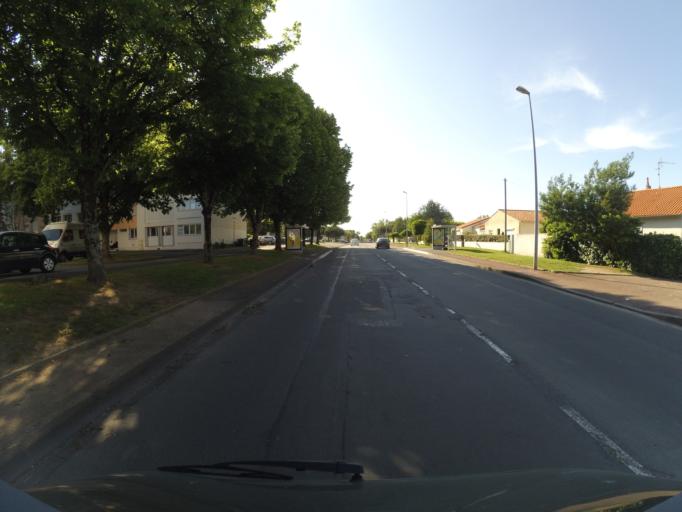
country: FR
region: Poitou-Charentes
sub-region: Departement de la Charente-Maritime
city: Royan
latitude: 45.6358
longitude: -1.0267
